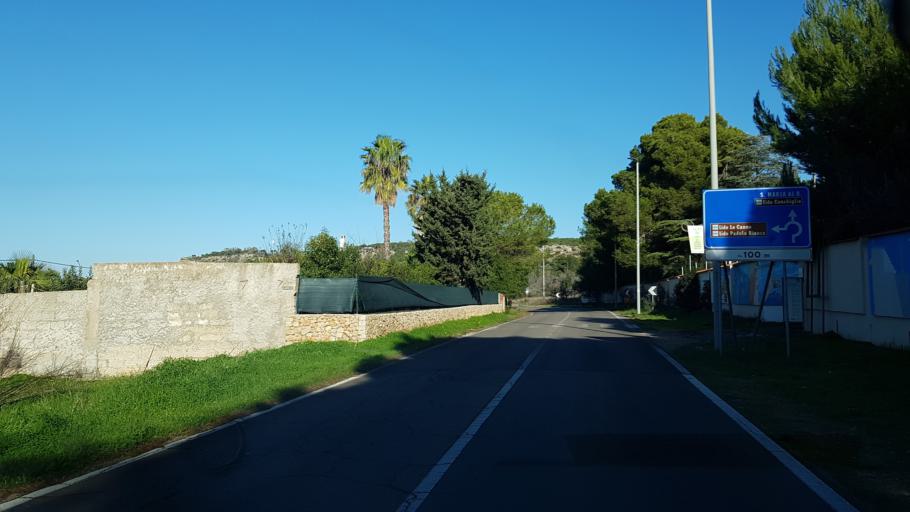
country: IT
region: Apulia
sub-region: Provincia di Lecce
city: Sannicola
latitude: 40.1019
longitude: 18.0198
